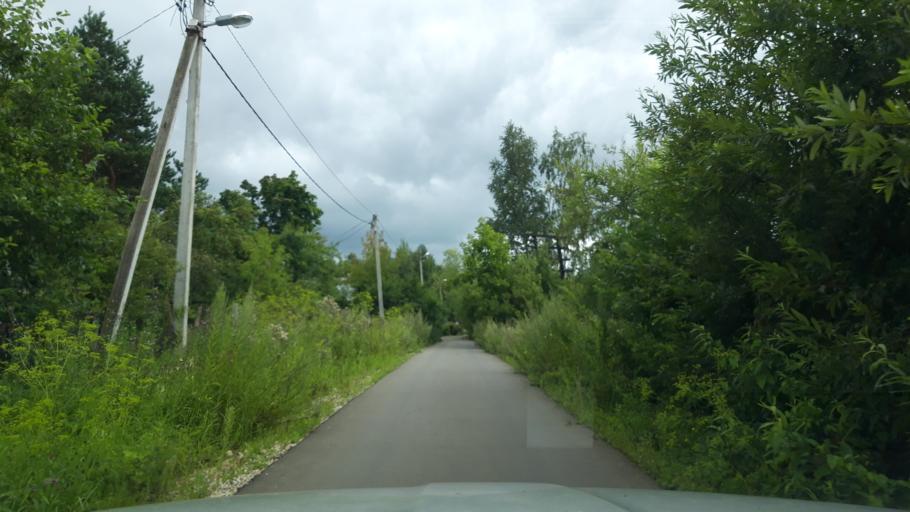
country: RU
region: Moskovskaya
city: Povarovo
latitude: 56.0680
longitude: 37.0732
